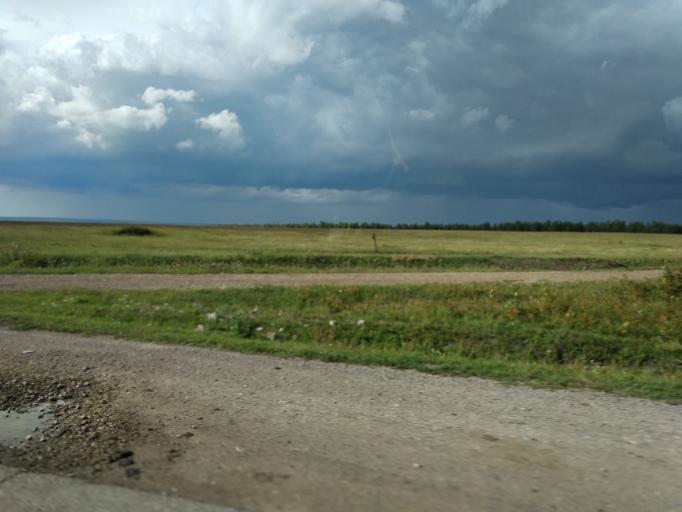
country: RU
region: Irkutsk
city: Bayanday
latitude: 52.9718
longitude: 105.3055
